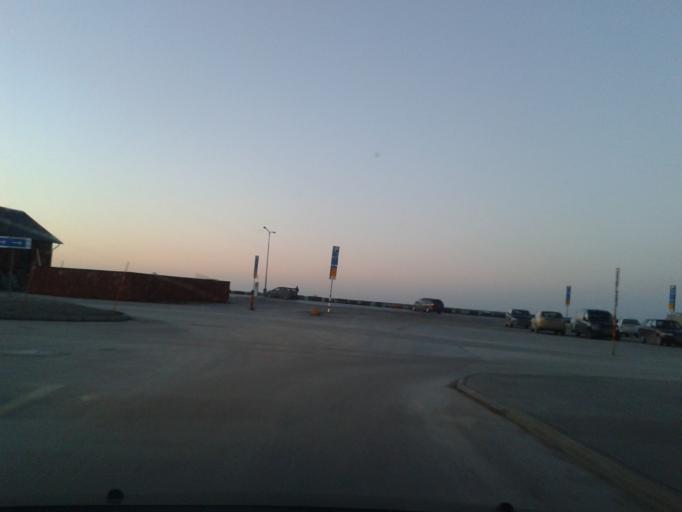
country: SE
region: Gotland
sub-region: Gotland
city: Visby
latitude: 57.6396
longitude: 18.2870
